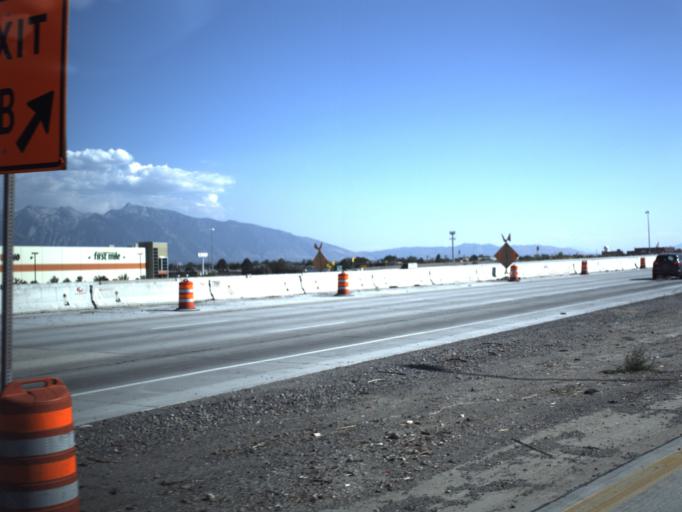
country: US
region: Utah
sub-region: Salt Lake County
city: Taylorsville
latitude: 40.7294
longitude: -111.9506
